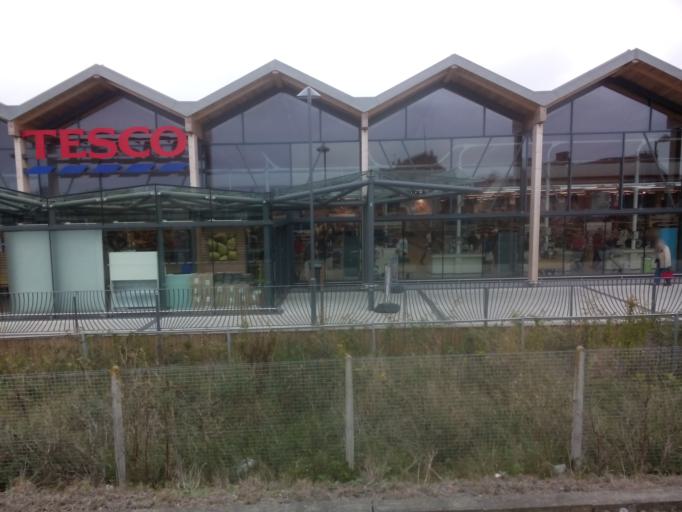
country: GB
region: England
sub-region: Norfolk
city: Sheringham
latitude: 52.9414
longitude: 1.2111
